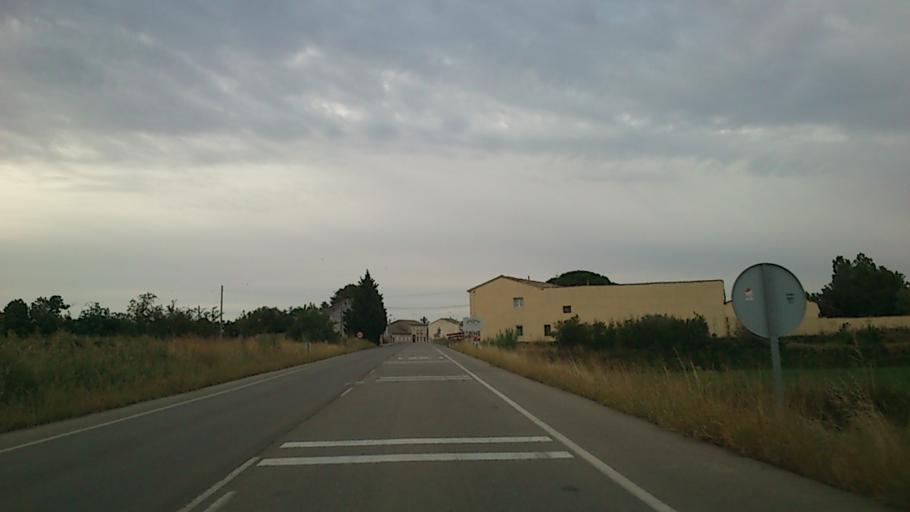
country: ES
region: Aragon
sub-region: Provincia de Zaragoza
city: Villanueva de Gallego
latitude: 41.7647
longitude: -0.7956
